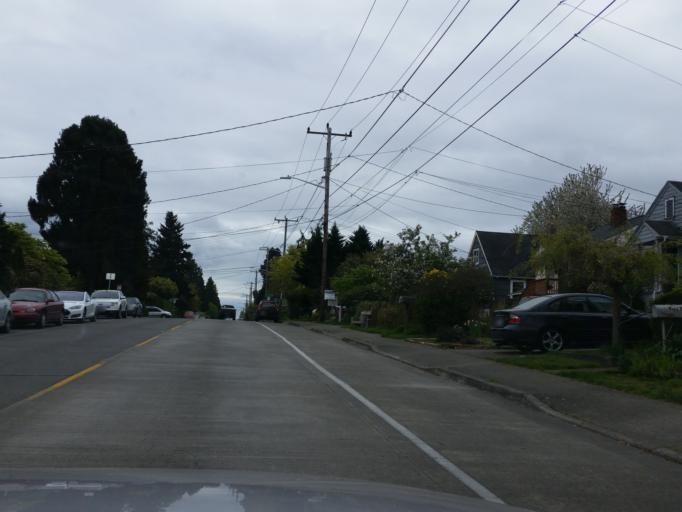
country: US
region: Washington
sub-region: King County
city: Shoreline
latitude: 47.6953
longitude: -122.3662
